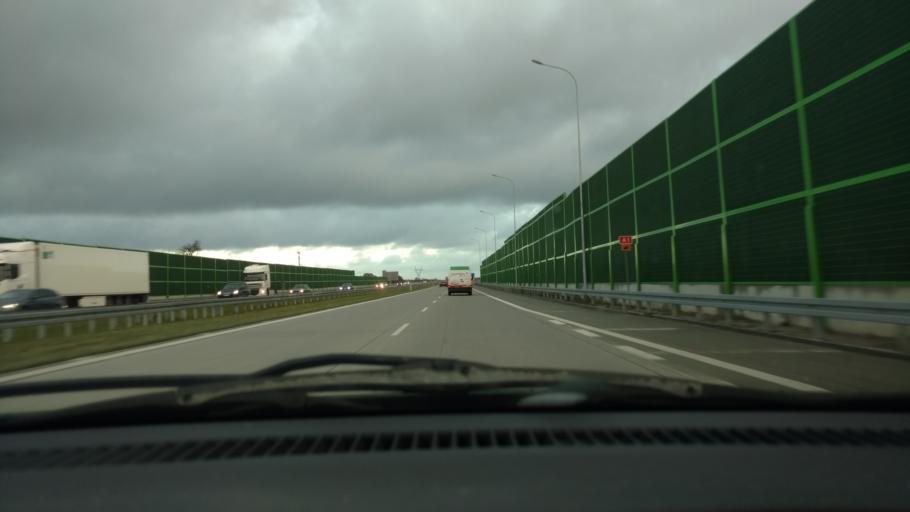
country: PL
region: Lodz Voivodeship
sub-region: Powiat lodzki wschodni
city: Brojce
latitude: 51.6809
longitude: 19.5929
